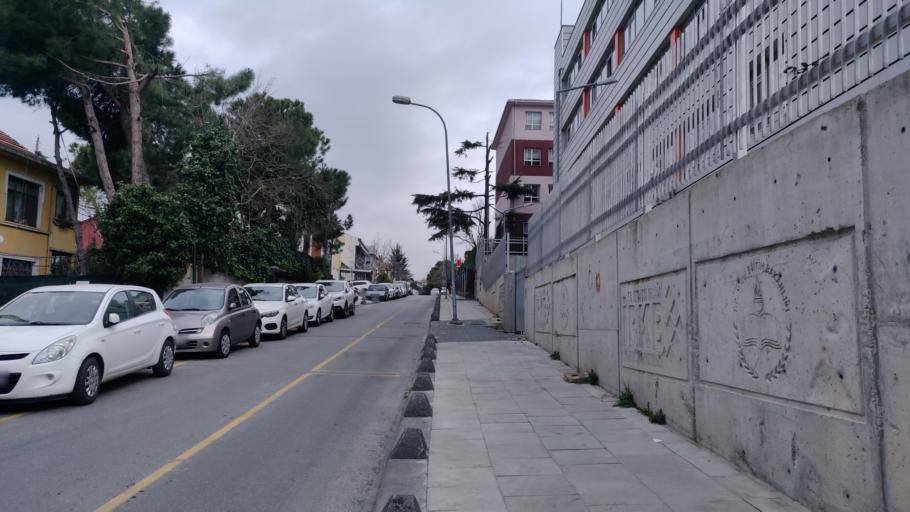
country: TR
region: Istanbul
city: UEskuedar
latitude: 41.0092
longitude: 29.0353
